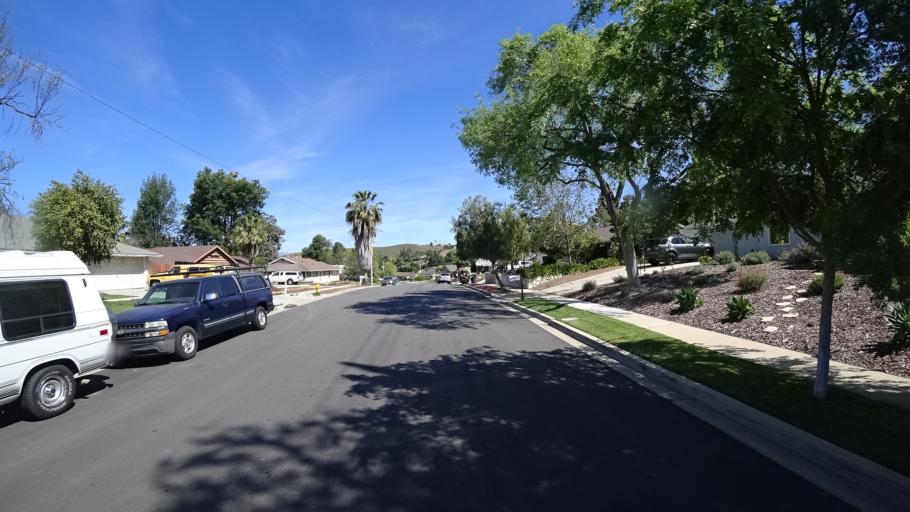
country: US
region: California
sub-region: Ventura County
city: Thousand Oaks
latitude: 34.2221
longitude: -118.8656
